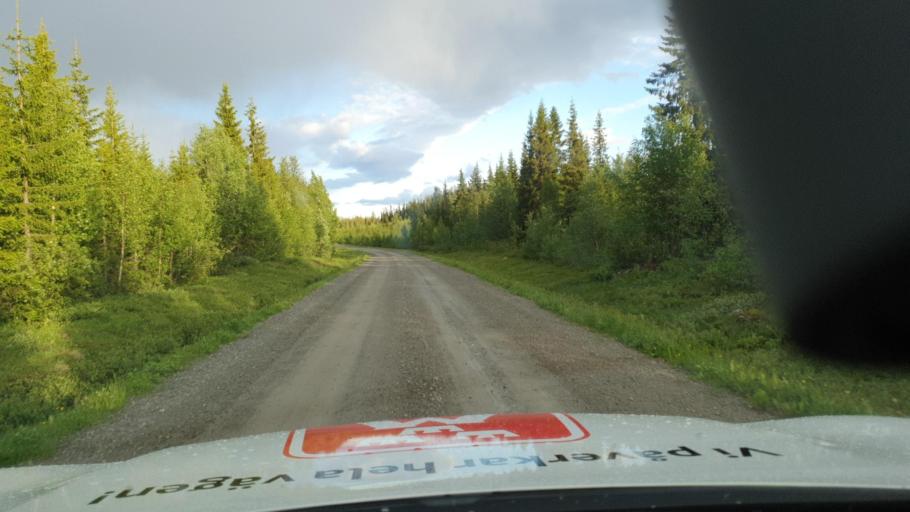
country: SE
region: Vaesterbotten
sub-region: Storumans Kommun
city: Storuman
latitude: 64.7731
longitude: 17.0420
